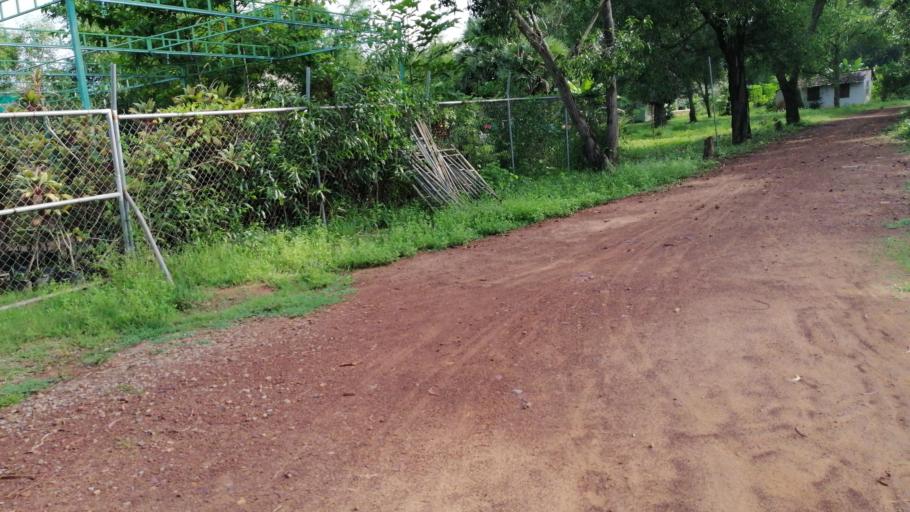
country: KH
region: Siem Reap
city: Siem Reap
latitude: 13.3492
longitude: 103.8183
